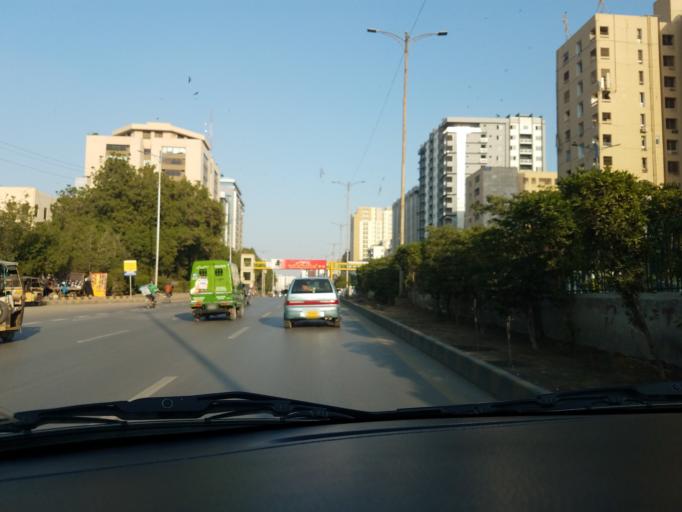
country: PK
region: Sindh
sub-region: Karachi District
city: Karachi
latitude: 24.8606
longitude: 67.0638
